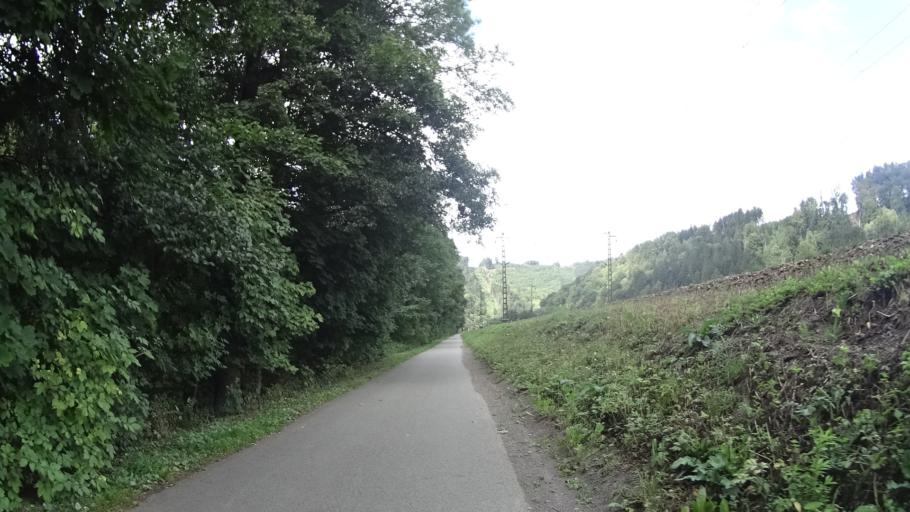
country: CZ
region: Pardubicky
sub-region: Okres Usti nad Orlici
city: Usti nad Orlici
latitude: 49.9736
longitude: 16.3482
